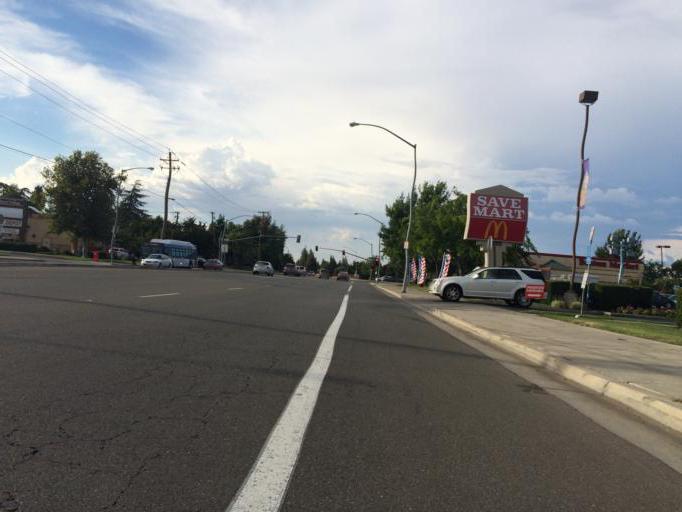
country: US
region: California
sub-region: Fresno County
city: Clovis
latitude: 36.8507
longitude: -119.7745
